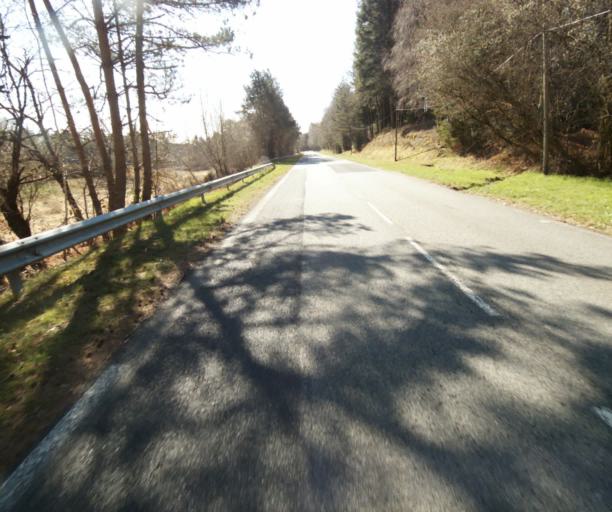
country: FR
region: Limousin
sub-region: Departement de la Correze
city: Correze
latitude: 45.2831
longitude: 1.9222
